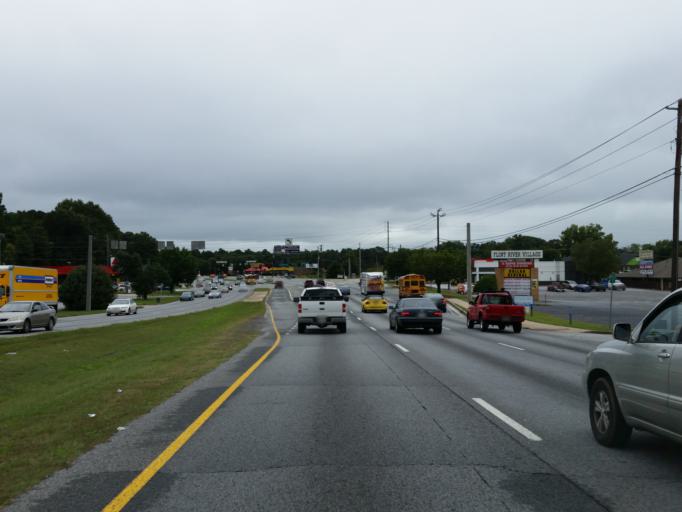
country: US
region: Georgia
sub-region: Clayton County
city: Jonesboro
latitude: 33.5196
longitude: -84.3637
